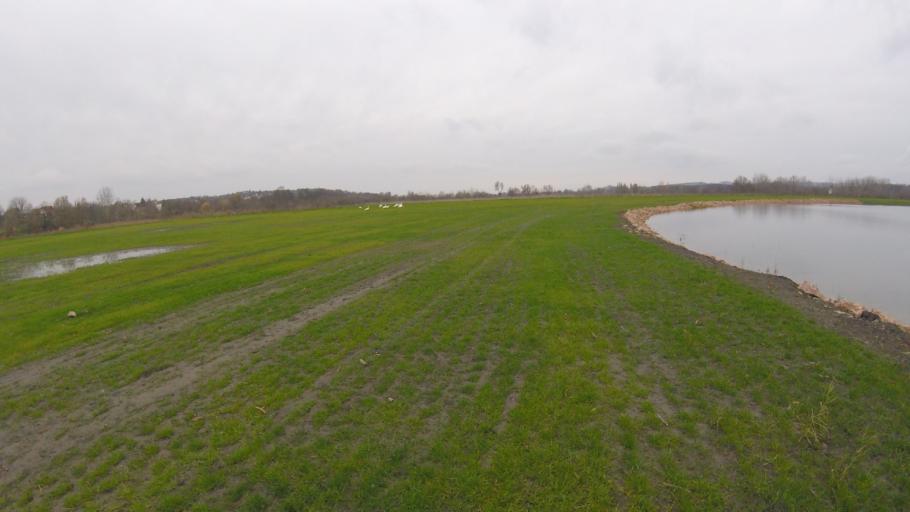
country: HU
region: Komarom-Esztergom
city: Tata
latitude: 47.6569
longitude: 18.3003
